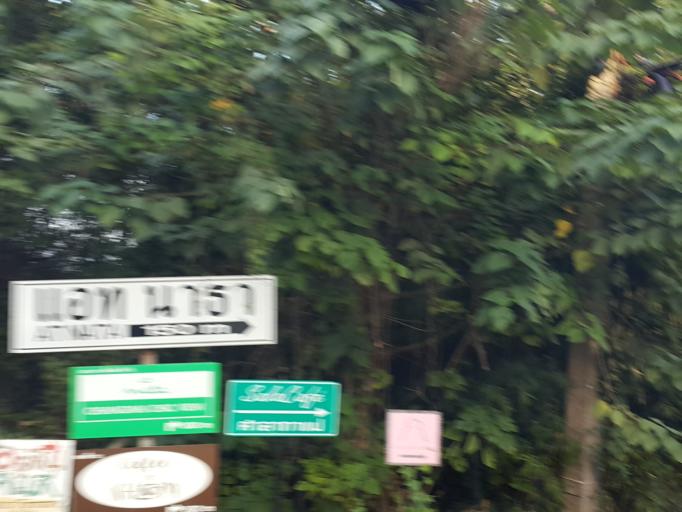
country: TH
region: Chiang Mai
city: Chiang Mai
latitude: 18.9089
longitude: 98.9057
